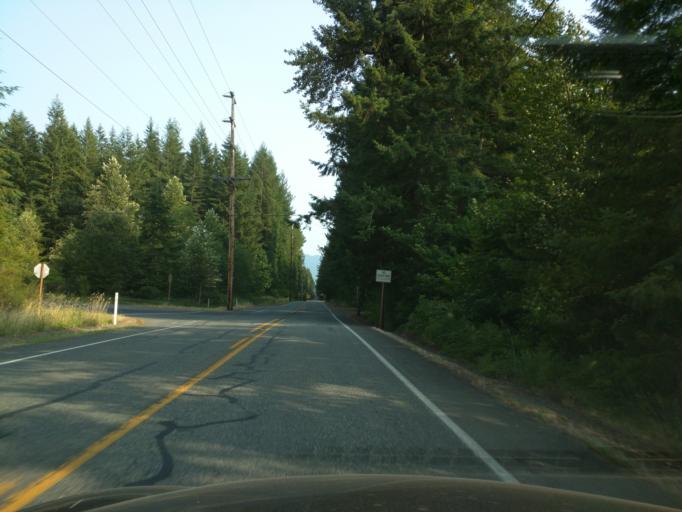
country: US
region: Washington
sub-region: Whatcom County
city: Peaceful Valley
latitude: 48.9576
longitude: -122.1577
